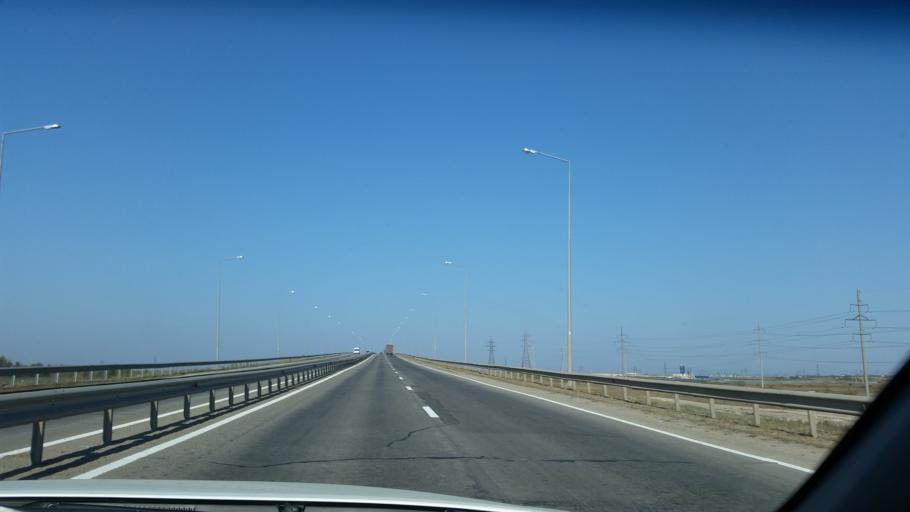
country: KZ
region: Astana Qalasy
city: Astana
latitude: 51.2223
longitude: 71.3225
